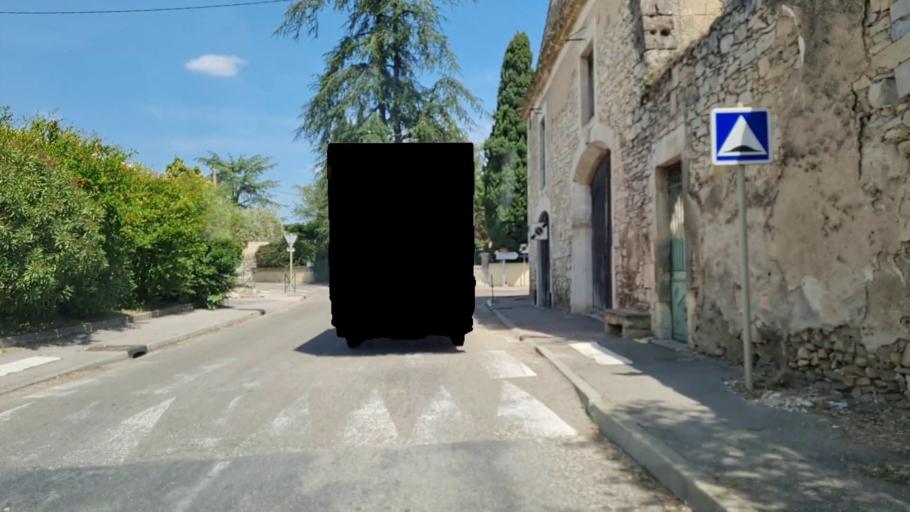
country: FR
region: Languedoc-Roussillon
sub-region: Departement du Gard
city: Saint-Gervasy
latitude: 43.8778
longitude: 4.4671
